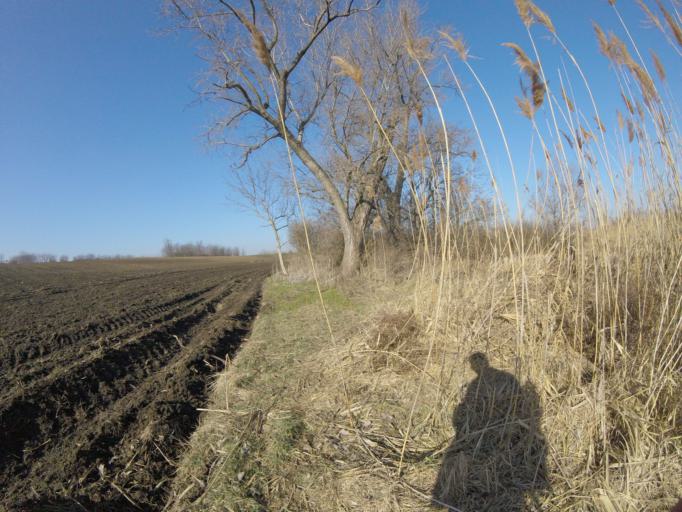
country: HU
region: Komarom-Esztergom
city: Csaszar
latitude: 47.5340
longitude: 18.1876
